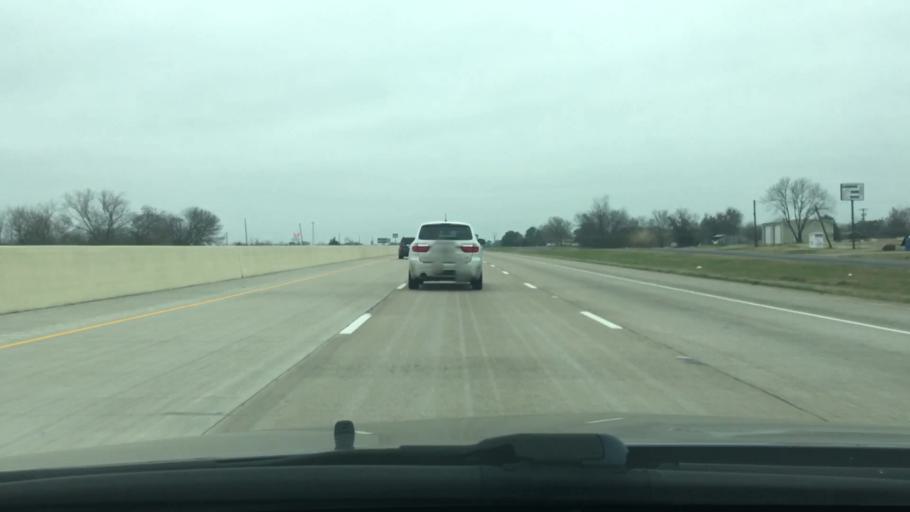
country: US
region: Texas
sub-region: Navarro County
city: Corsicana
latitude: 32.0186
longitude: -96.4383
